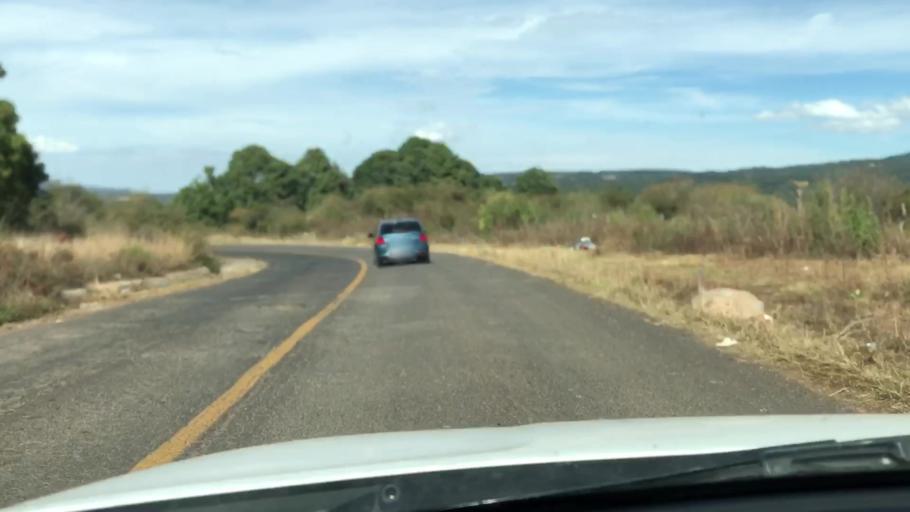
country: MX
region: Jalisco
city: Chiquilistlan
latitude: 20.1399
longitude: -103.7170
